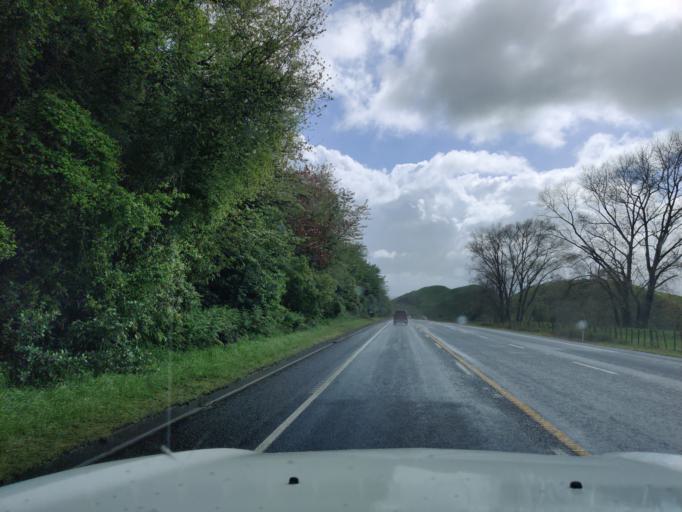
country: NZ
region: Waikato
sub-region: Matamata-Piako District
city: Matamata
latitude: -37.9794
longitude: 175.7384
